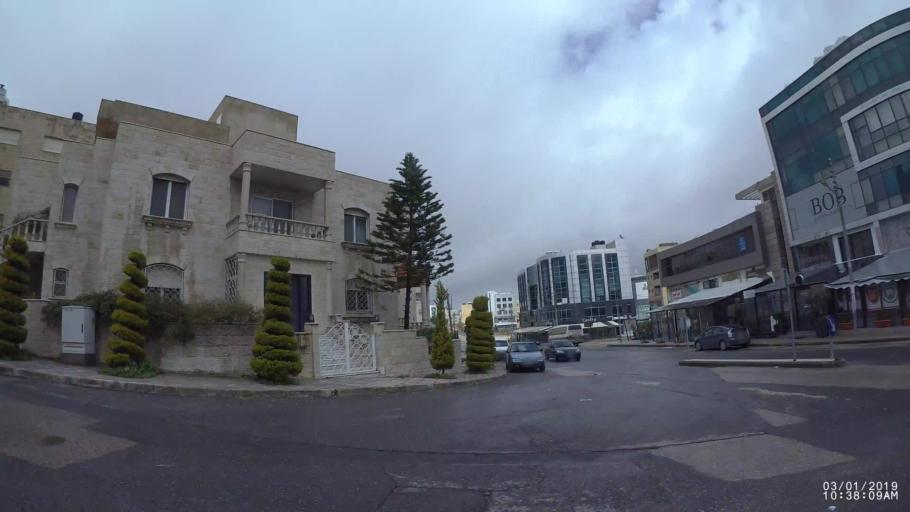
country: JO
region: Amman
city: Wadi as Sir
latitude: 31.9542
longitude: 35.8533
